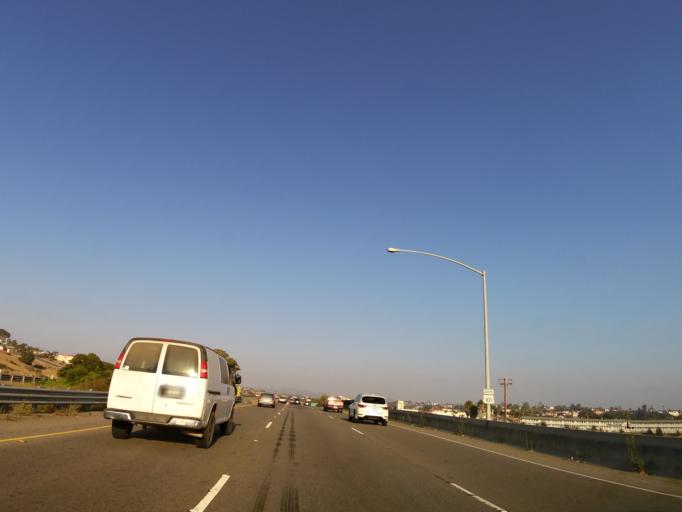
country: US
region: California
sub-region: San Luis Obispo County
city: Pismo Beach
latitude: 35.1387
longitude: -120.6337
